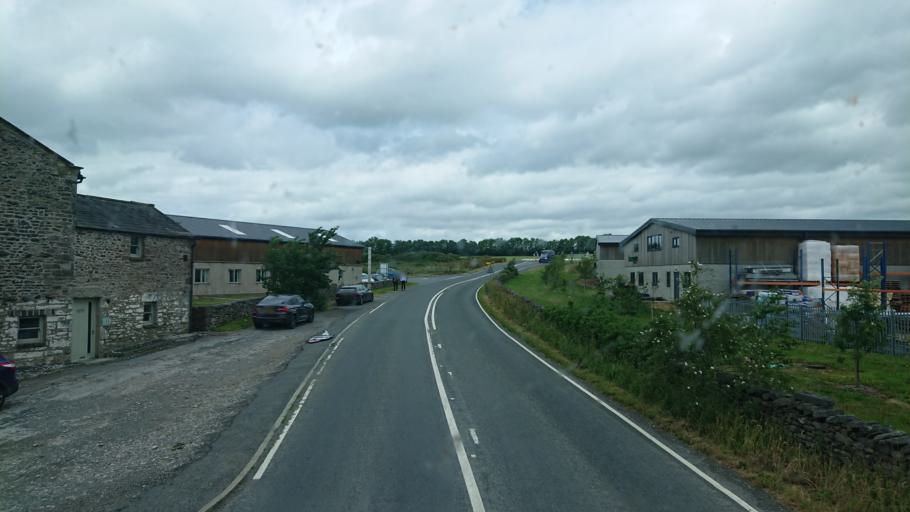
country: GB
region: England
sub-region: Cumbria
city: Milnthorpe
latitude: 54.2319
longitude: -2.7137
